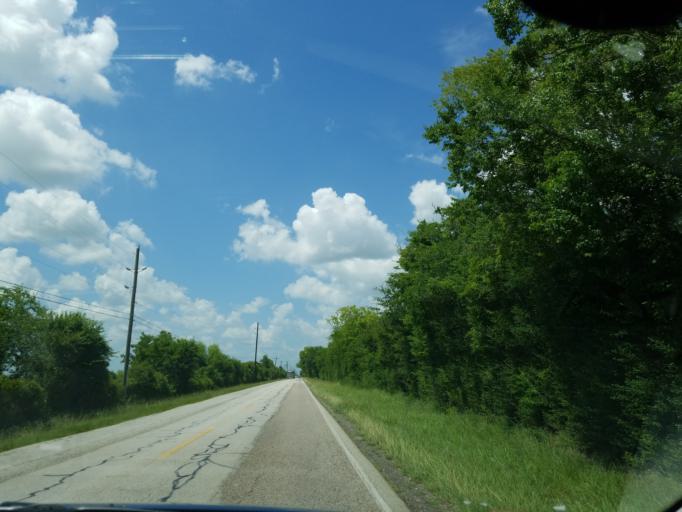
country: US
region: Texas
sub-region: Harris County
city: Katy
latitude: 29.8698
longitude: -95.8072
